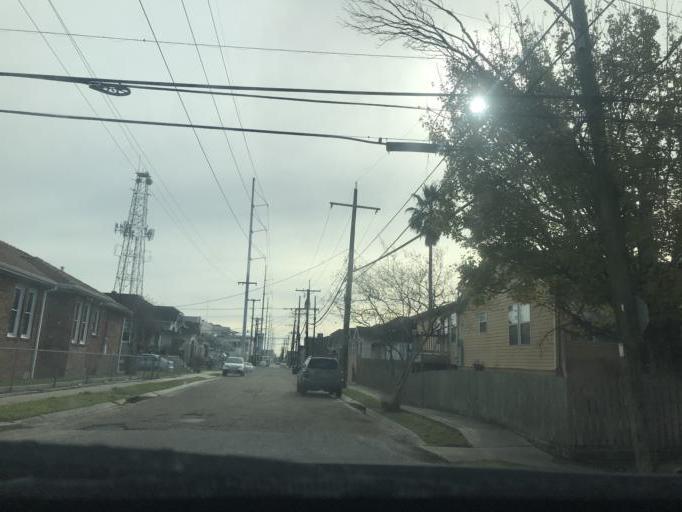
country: US
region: Louisiana
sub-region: Orleans Parish
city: New Orleans
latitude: 29.9611
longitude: -90.1048
